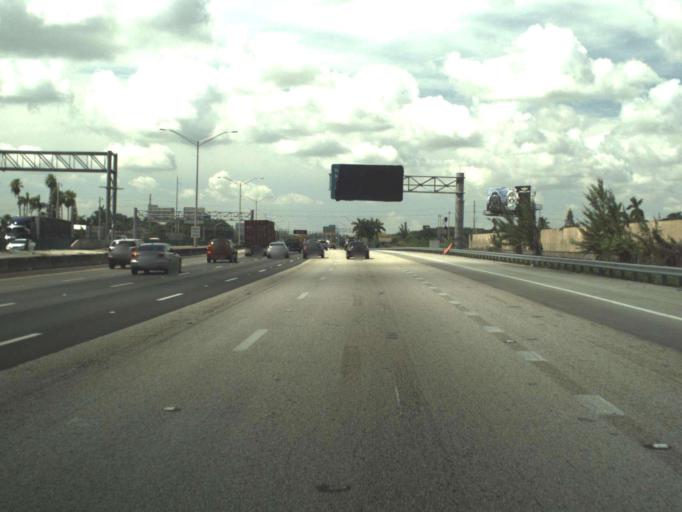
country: US
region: Florida
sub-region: Broward County
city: Pembroke Park
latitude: 25.9771
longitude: -80.1663
